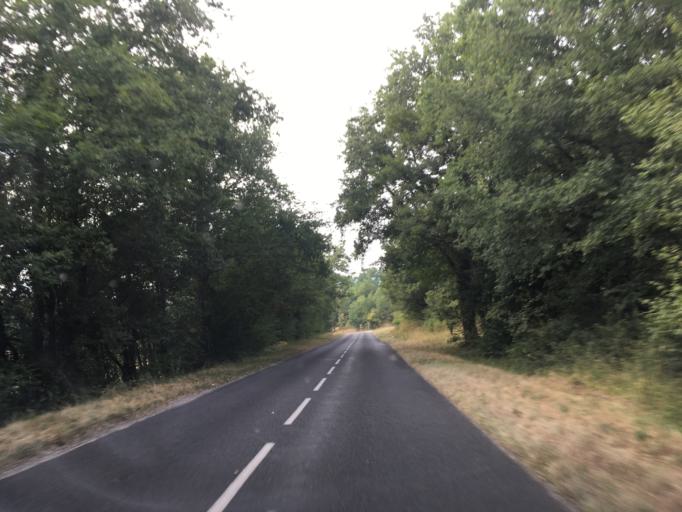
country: FR
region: Midi-Pyrenees
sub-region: Departement du Lot
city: Souillac
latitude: 44.8475
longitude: 1.5421
